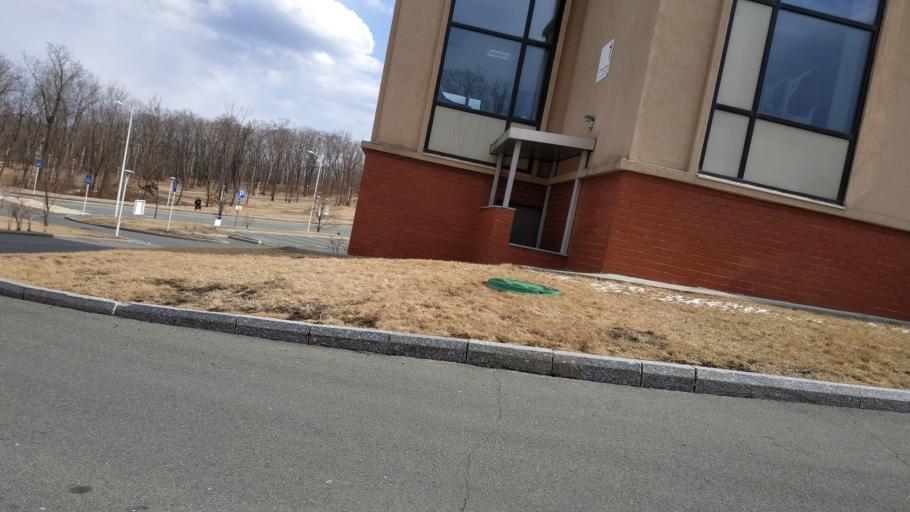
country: RU
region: Primorskiy
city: Russkiy
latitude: 43.0284
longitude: 131.8888
